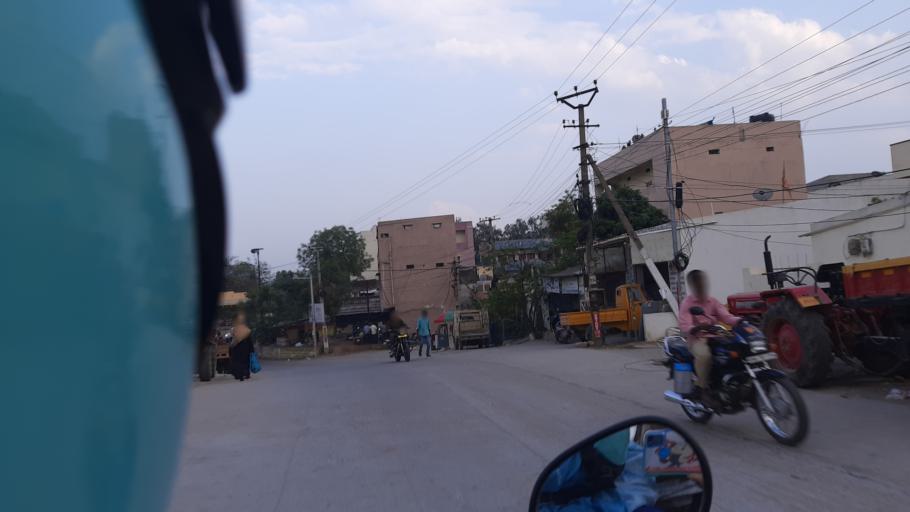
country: IN
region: Telangana
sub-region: Rangareddi
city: Kukatpalli
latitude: 17.4952
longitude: 78.4311
